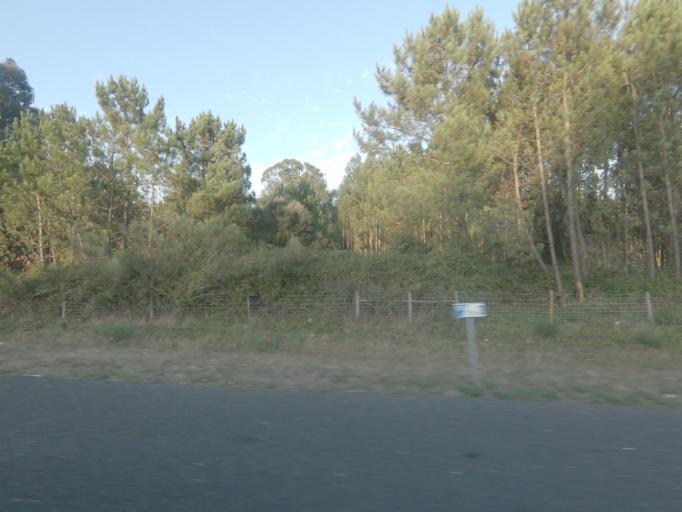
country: PT
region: Santarem
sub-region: Ourem
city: Fatima
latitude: 39.6310
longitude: -8.6982
